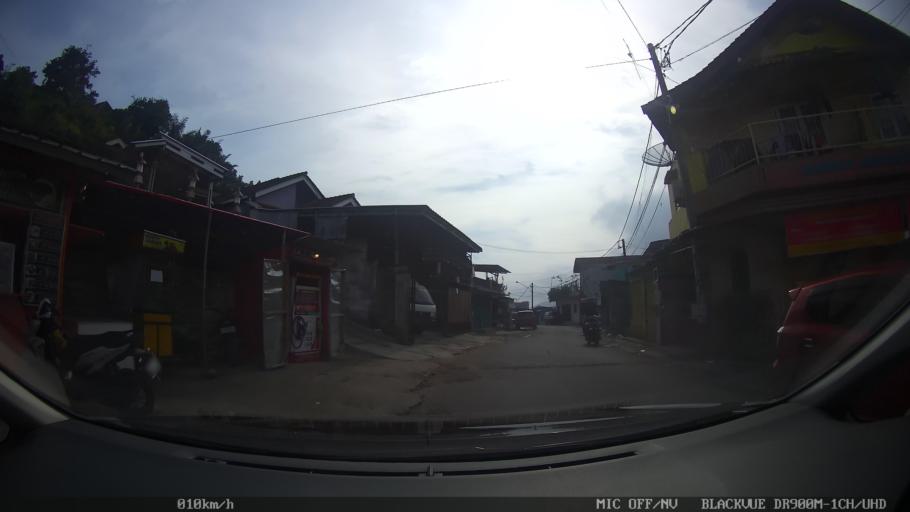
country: ID
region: Lampung
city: Bandarlampung
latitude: -5.4138
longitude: 105.2632
